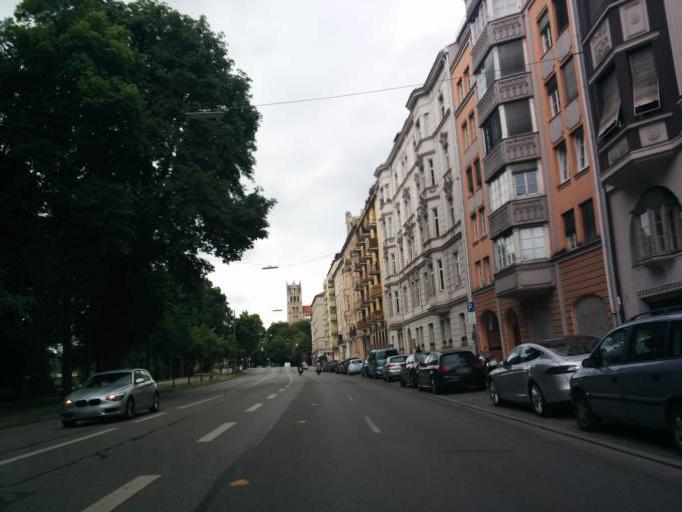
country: DE
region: Bavaria
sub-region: Upper Bavaria
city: Munich
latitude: 48.1288
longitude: 11.5780
